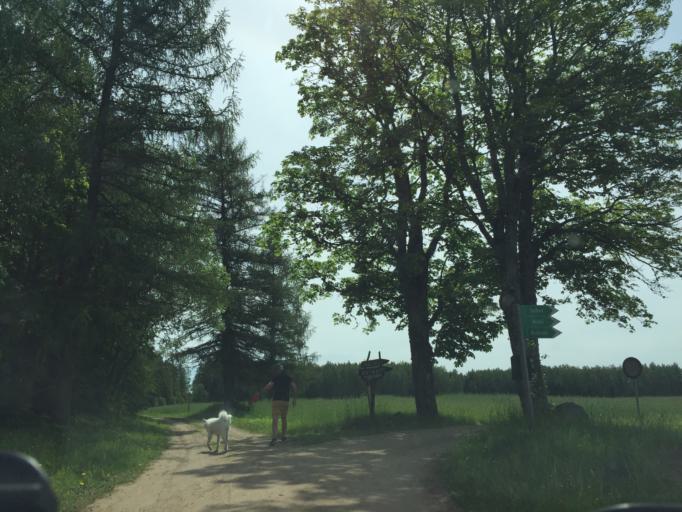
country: LV
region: Koceni
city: Koceni
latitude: 57.4452
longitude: 25.2809
